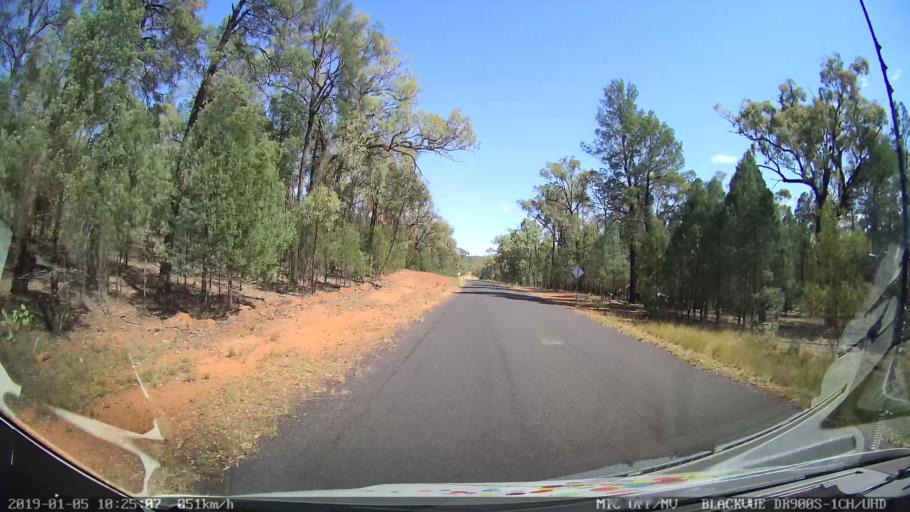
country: AU
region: New South Wales
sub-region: Gilgandra
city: Gilgandra
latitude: -31.5638
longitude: 148.9612
